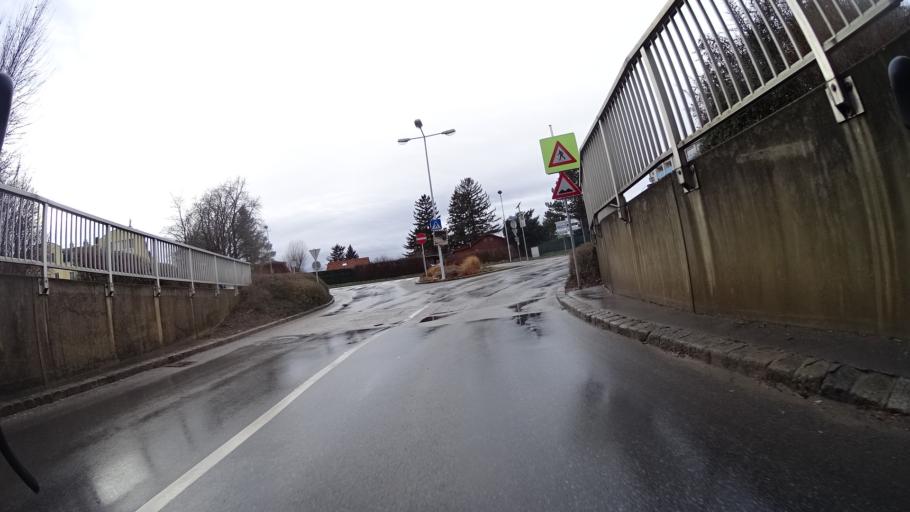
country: AT
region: Lower Austria
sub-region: Politischer Bezirk Korneuburg
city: Korneuburg
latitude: 48.3416
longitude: 16.3299
